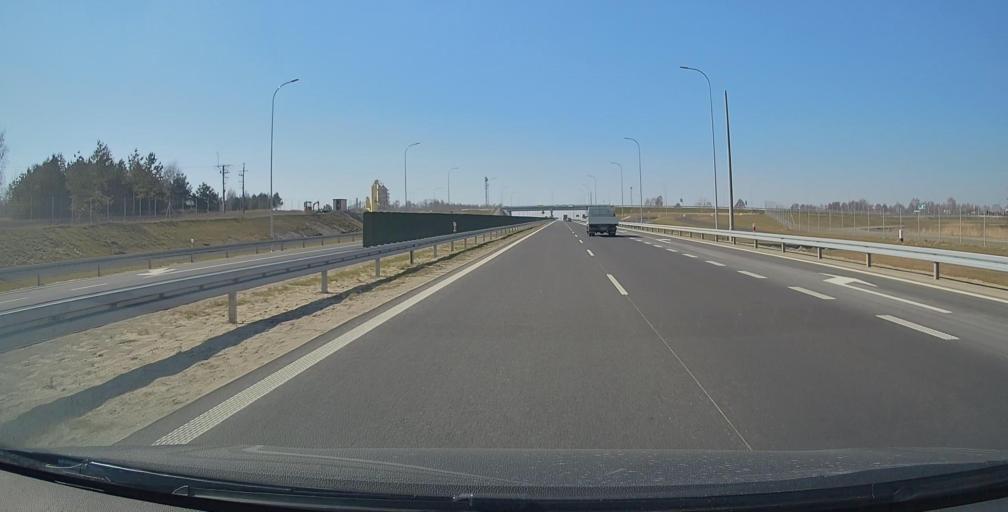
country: PL
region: Subcarpathian Voivodeship
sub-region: Powiat rzeszowski
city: Gorno
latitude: 50.3039
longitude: 22.1359
